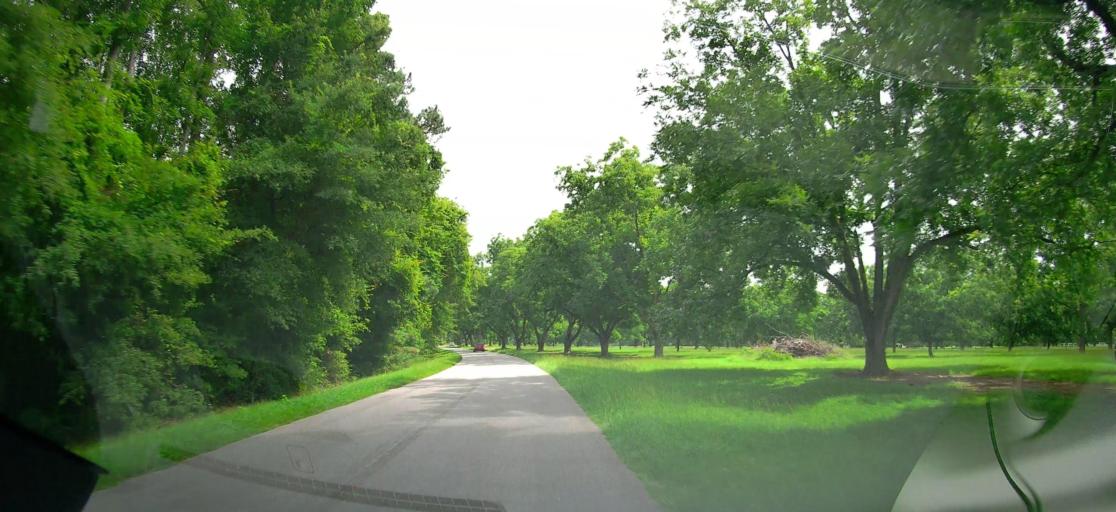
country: US
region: Georgia
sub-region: Peach County
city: Byron
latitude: 32.6385
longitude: -83.7404
